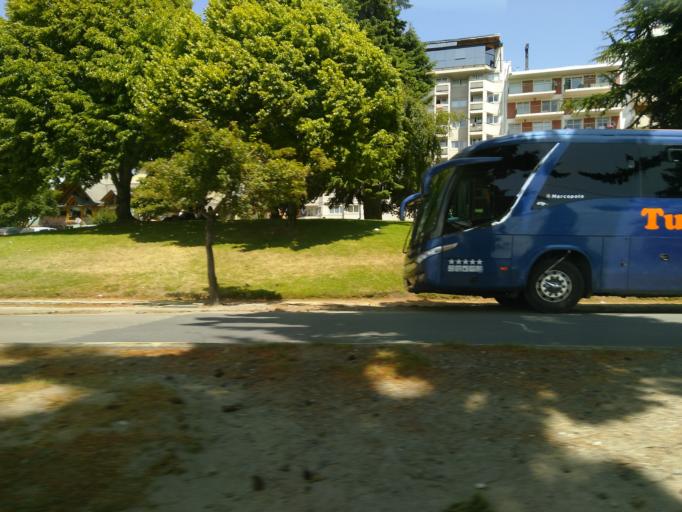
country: AR
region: Rio Negro
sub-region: Departamento de Bariloche
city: San Carlos de Bariloche
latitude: -41.1326
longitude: -71.3041
